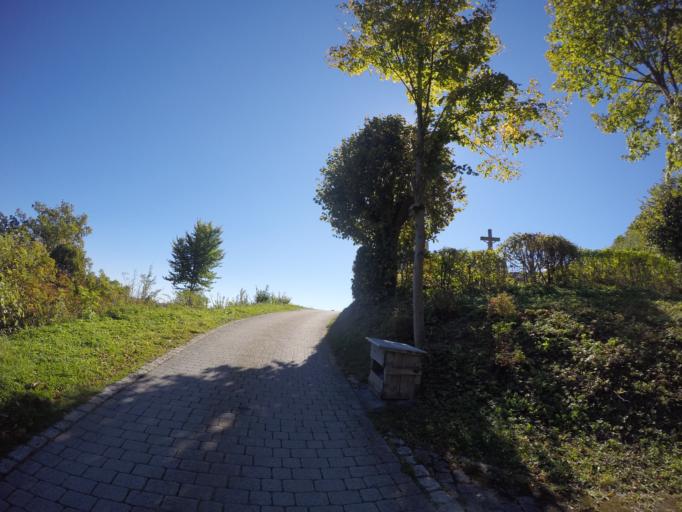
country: DE
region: Bavaria
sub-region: Upper Franconia
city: Weilersbach
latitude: 49.7563
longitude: 11.1359
